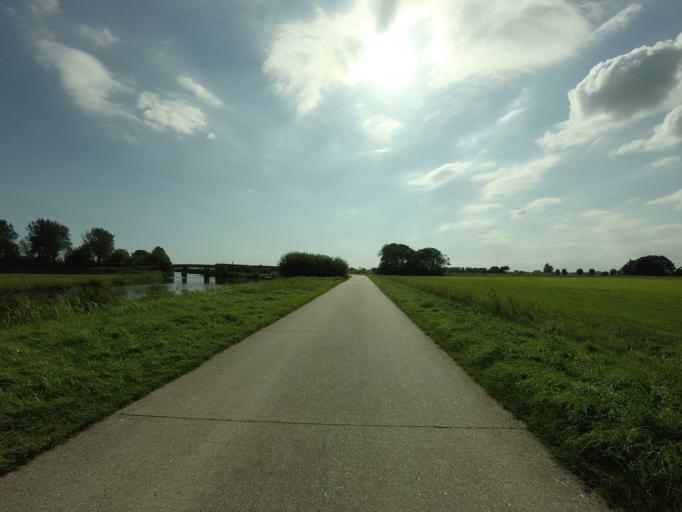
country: NL
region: Friesland
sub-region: Sudwest Fryslan
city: Scharnegoutum
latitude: 53.0775
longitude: 5.6313
